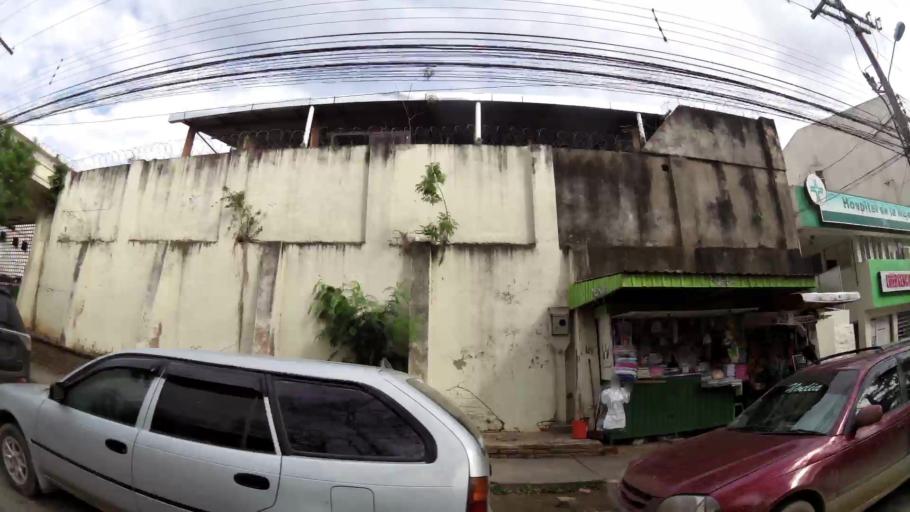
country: BO
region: Santa Cruz
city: Santa Cruz de la Sierra
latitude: -17.7781
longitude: -63.1867
